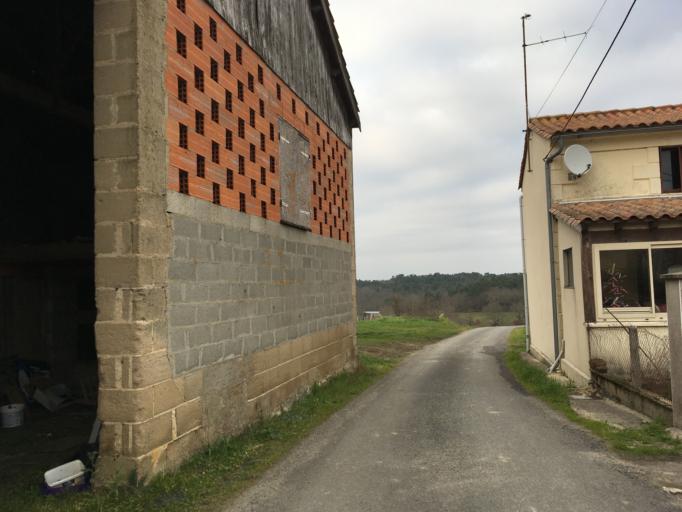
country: FR
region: Aquitaine
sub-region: Departement de la Gironde
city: Saint-Ciers-sur-Gironde
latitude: 45.3155
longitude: -0.6175
